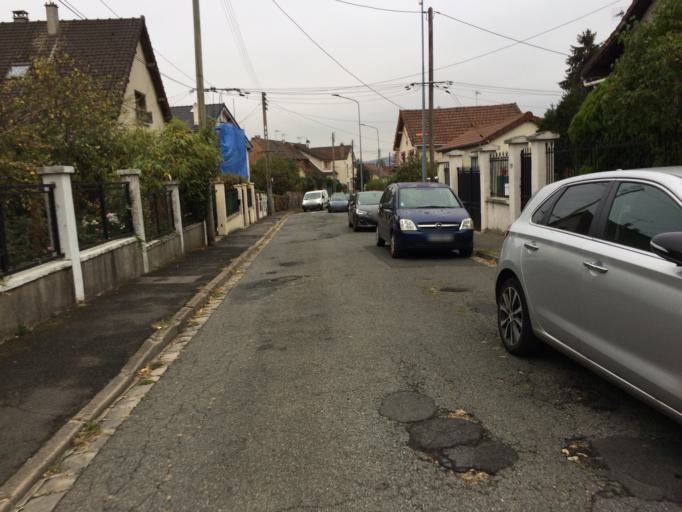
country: FR
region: Ile-de-France
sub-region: Departement de l'Essonne
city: Palaiseau
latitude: 48.7169
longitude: 2.2592
